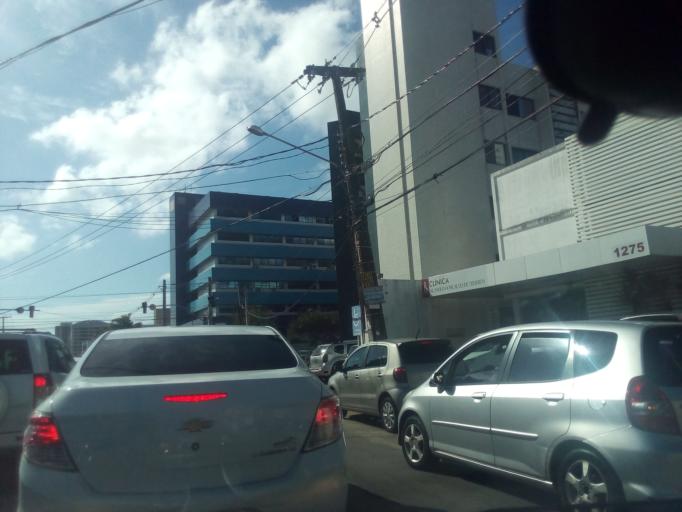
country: BR
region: Rio Grande do Norte
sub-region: Natal
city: Natal
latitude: -5.8229
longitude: -35.2160
